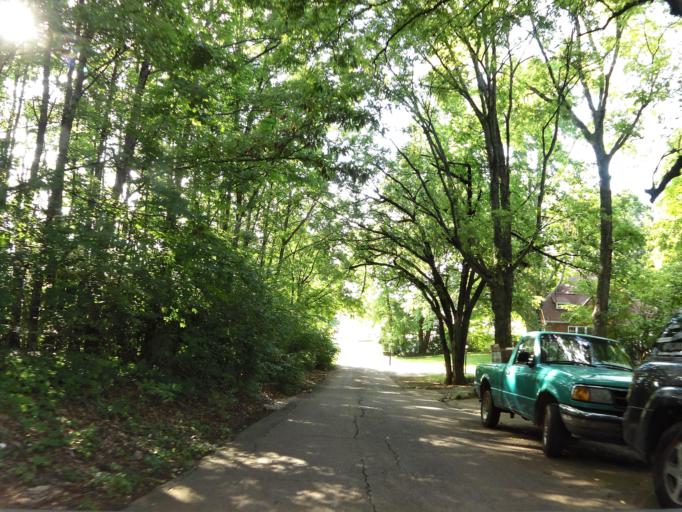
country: US
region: Tennessee
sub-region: Blount County
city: Maryville
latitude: 35.7539
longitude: -83.9612
